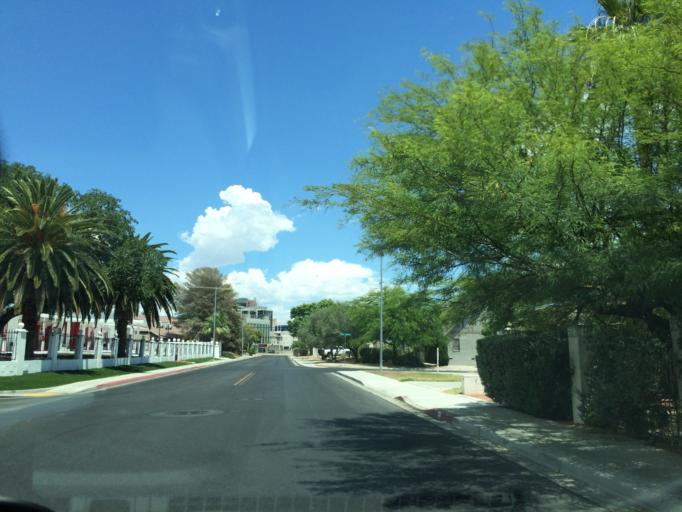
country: US
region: Nevada
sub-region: Clark County
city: Las Vegas
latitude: 36.1568
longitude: -115.1460
